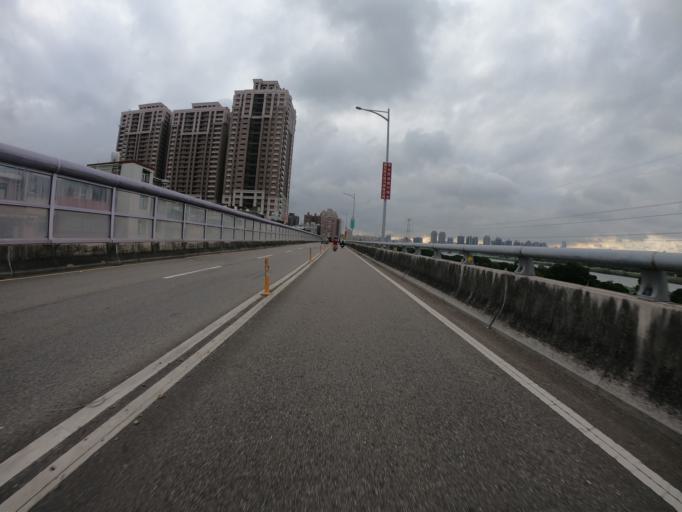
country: TW
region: Taipei
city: Taipei
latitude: 25.0172
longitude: 121.5081
